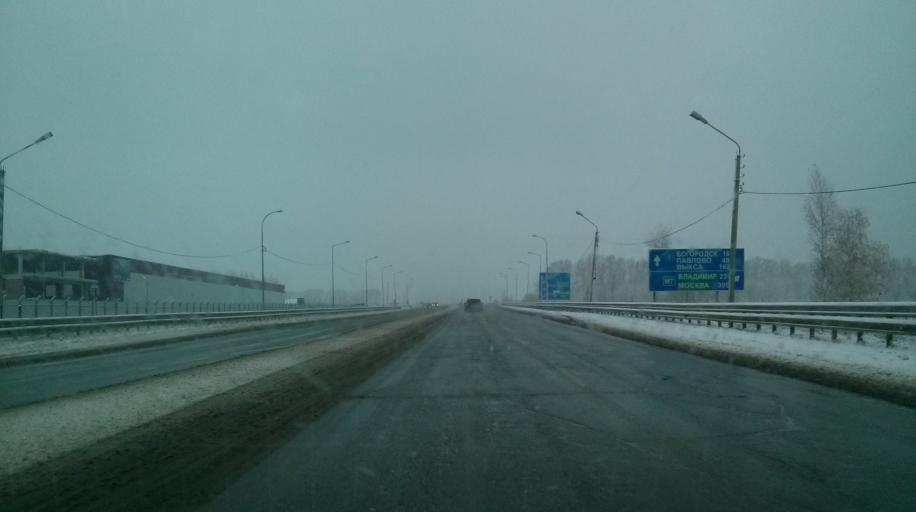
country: RU
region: Nizjnij Novgorod
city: Burevestnik
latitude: 56.1748
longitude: 43.7580
